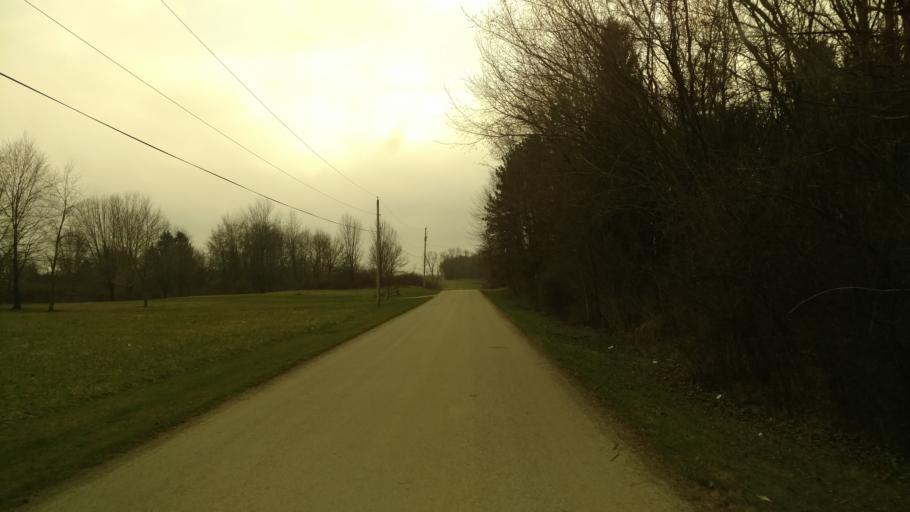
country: US
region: Ohio
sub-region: Morrow County
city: Mount Gilead
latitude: 40.5613
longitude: -82.7735
